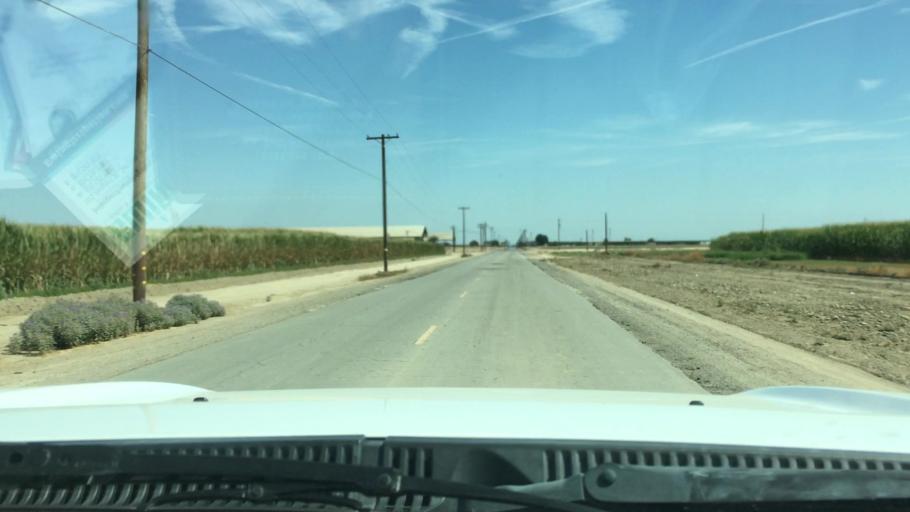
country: US
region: California
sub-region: Kern County
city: Buttonwillow
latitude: 35.4101
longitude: -119.3766
